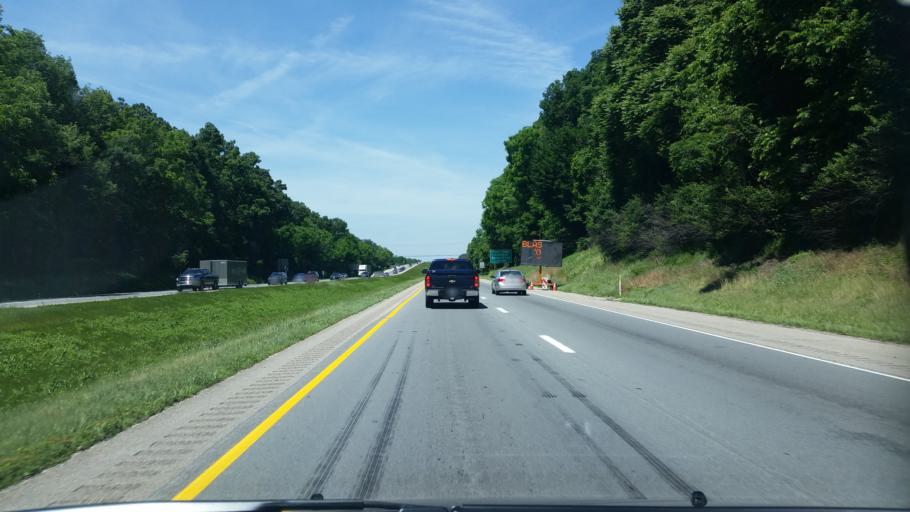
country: US
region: Pennsylvania
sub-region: Cumberland County
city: Carlisle
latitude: 40.1877
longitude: -77.1990
